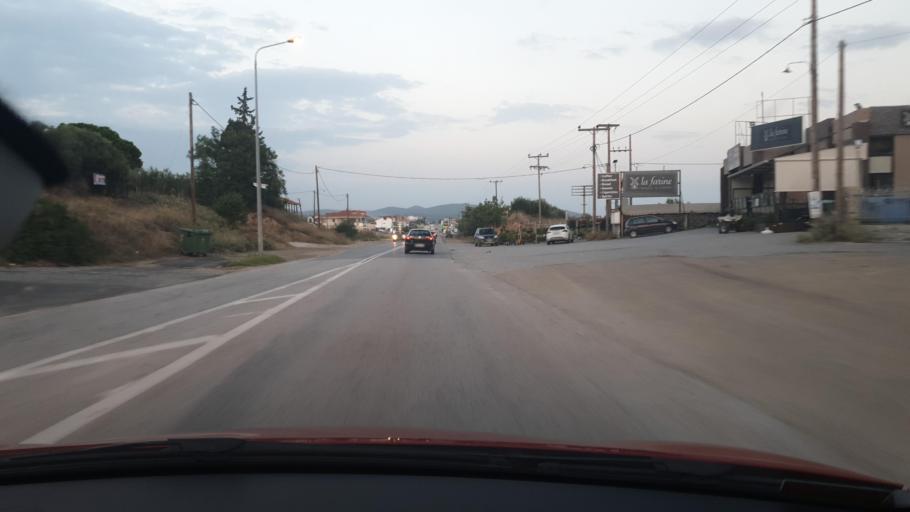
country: GR
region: Central Macedonia
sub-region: Nomos Chalkidikis
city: Kalyves Polygyrou
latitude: 40.2831
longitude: 23.3890
